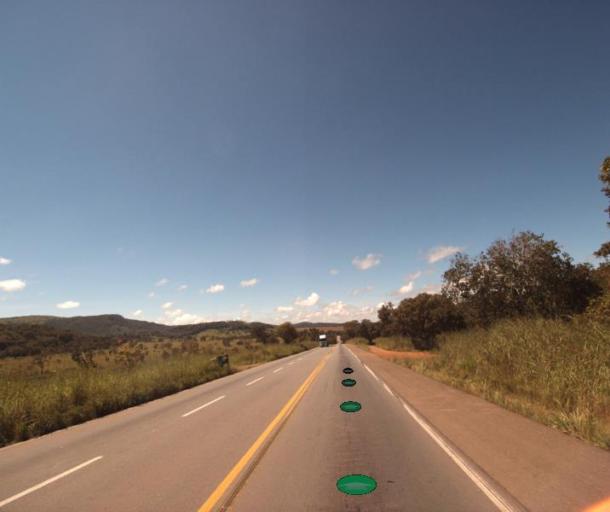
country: BR
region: Goias
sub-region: Jaragua
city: Jaragua
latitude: -15.6261
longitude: -49.3858
